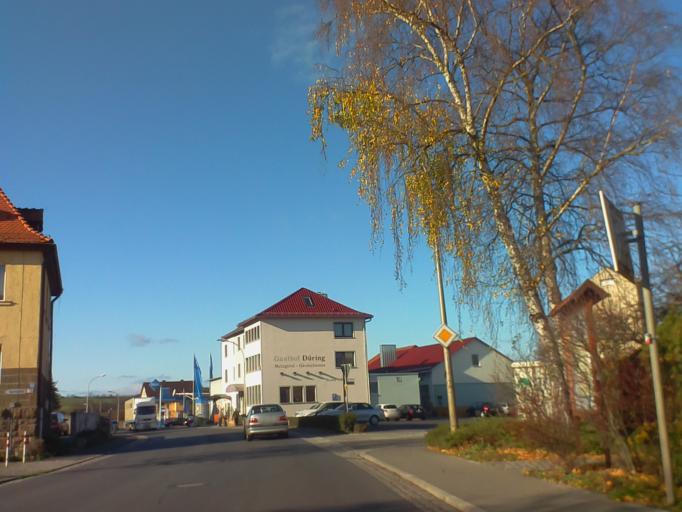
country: DE
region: Bavaria
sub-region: Regierungsbezirk Unterfranken
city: Saal an der Saale
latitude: 50.3172
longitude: 10.3550
